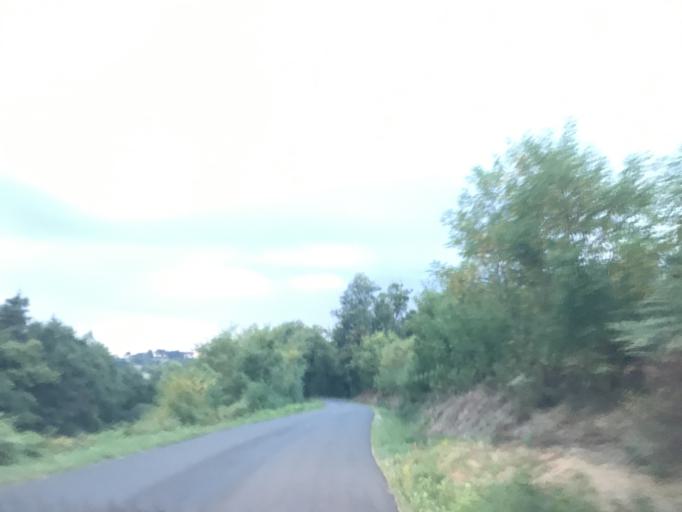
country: FR
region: Auvergne
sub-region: Departement du Puy-de-Dome
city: Escoutoux
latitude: 45.8085
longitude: 3.5670
